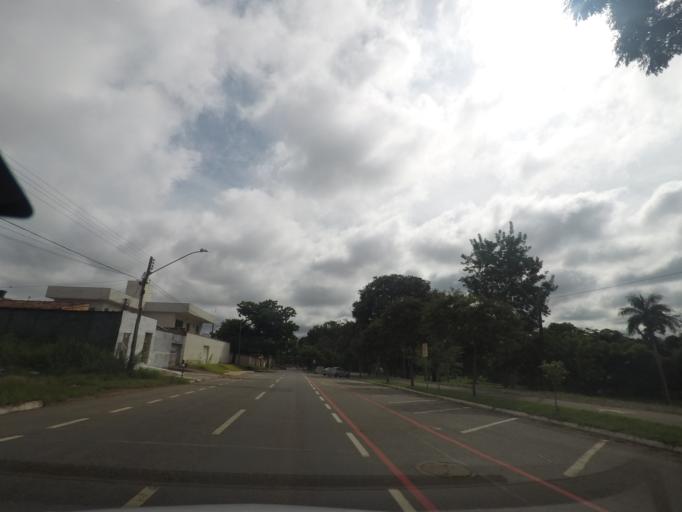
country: BR
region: Goias
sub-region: Goiania
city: Goiania
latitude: -16.7230
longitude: -49.2523
